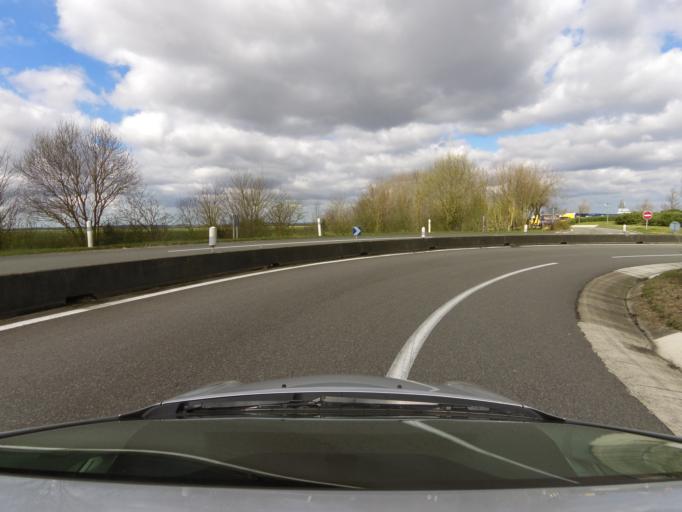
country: FR
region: Picardie
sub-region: Departement de la Somme
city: Sailly-Flibeaucourt
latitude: 50.1653
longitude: 1.7538
